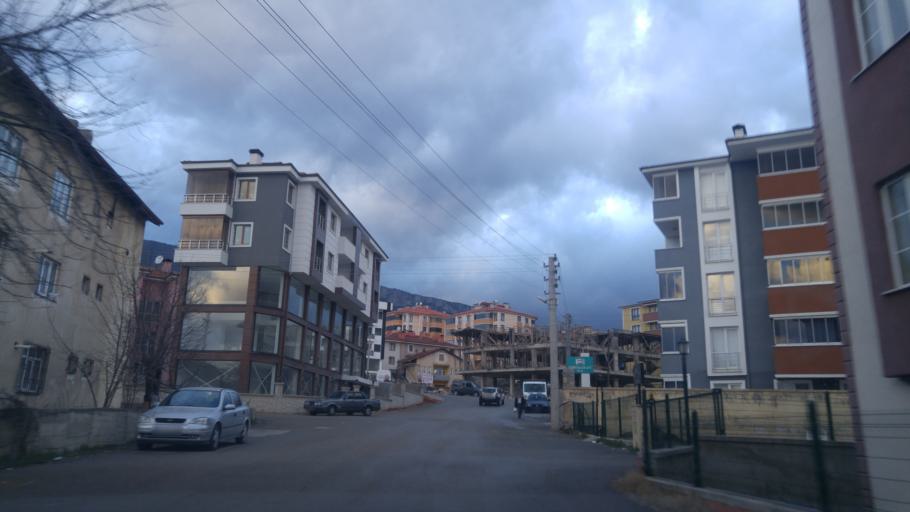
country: TR
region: Karabuk
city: Safranbolu
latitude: 41.2714
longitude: 32.6757
